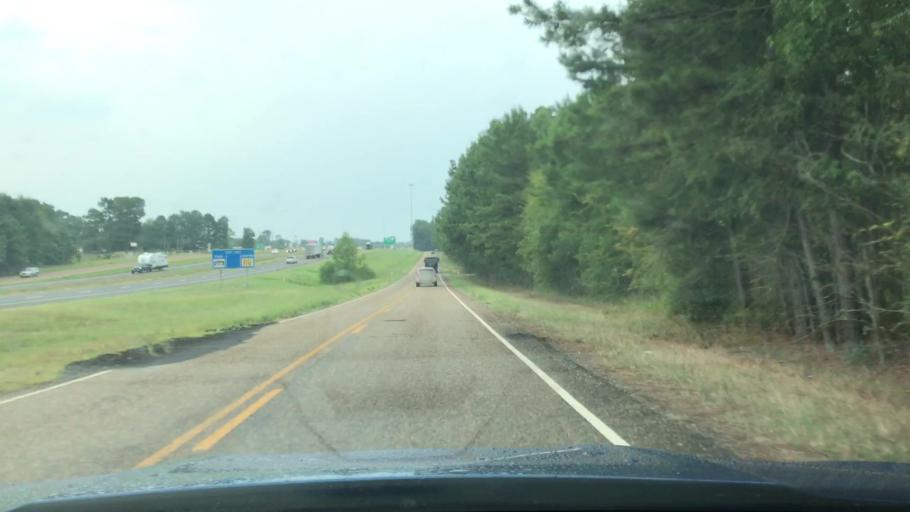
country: US
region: Texas
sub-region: Harrison County
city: Waskom
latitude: 32.4804
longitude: -94.0975
